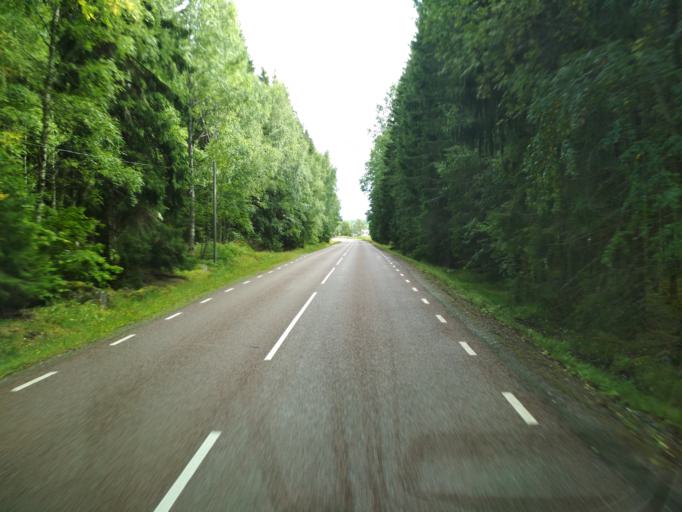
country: SE
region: Vaestmanland
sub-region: Surahammars Kommun
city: Ramnas
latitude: 59.8606
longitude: 16.0890
